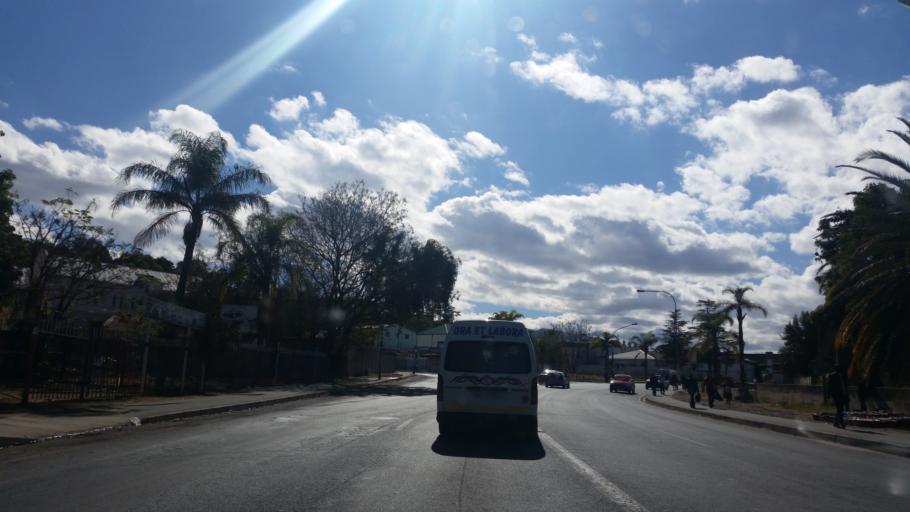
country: ZA
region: KwaZulu-Natal
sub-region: uThukela District Municipality
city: Ladysmith
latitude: -28.5565
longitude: 29.7851
